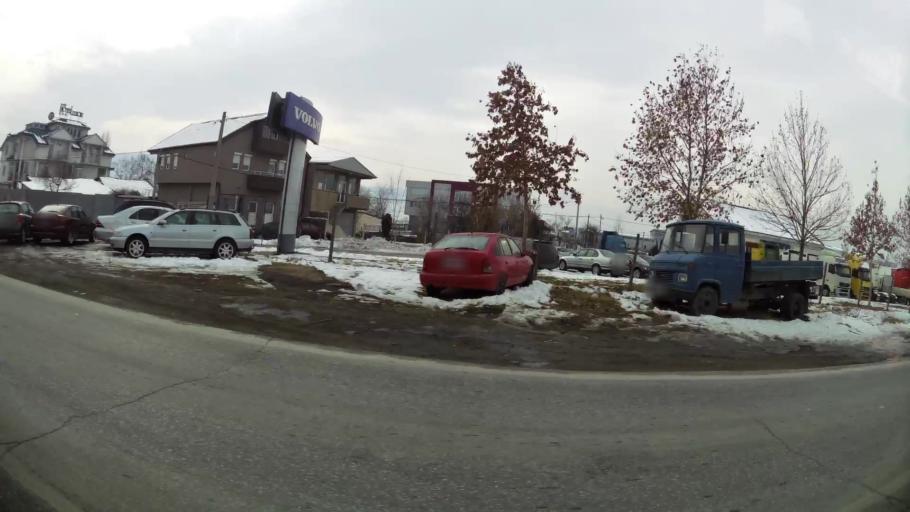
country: MK
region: Suto Orizari
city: Suto Orizare
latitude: 42.0317
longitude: 21.4044
